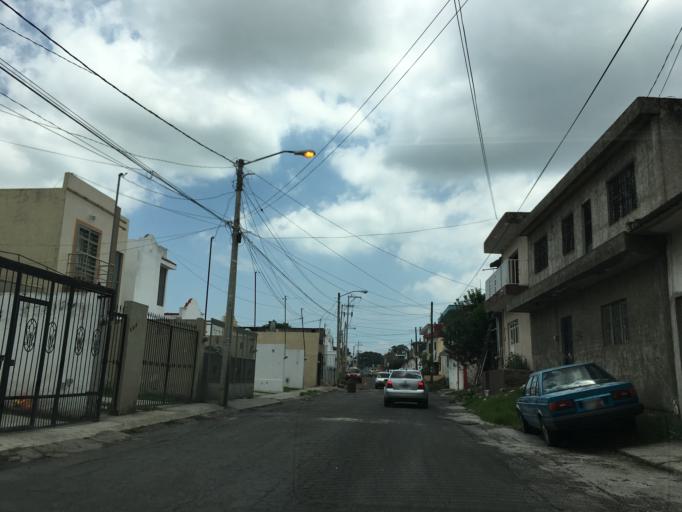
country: MX
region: Nayarit
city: Xalisco
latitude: 21.4737
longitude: -104.8878
